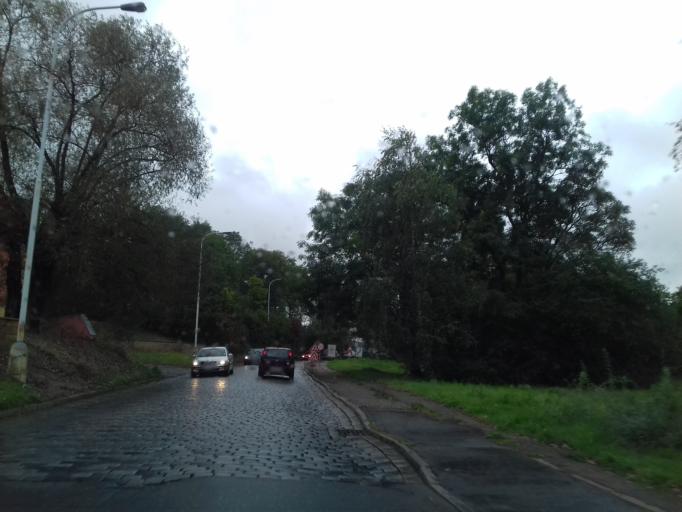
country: CZ
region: Praha
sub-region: Praha 1
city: Mala Strana
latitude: 50.0591
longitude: 14.3772
